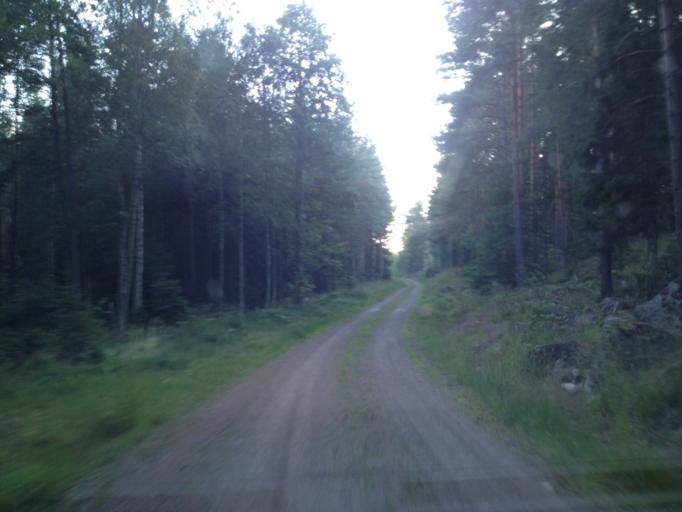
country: SE
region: Kalmar
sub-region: Vasterviks Kommun
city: Overum
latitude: 57.9980
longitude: 16.1438
